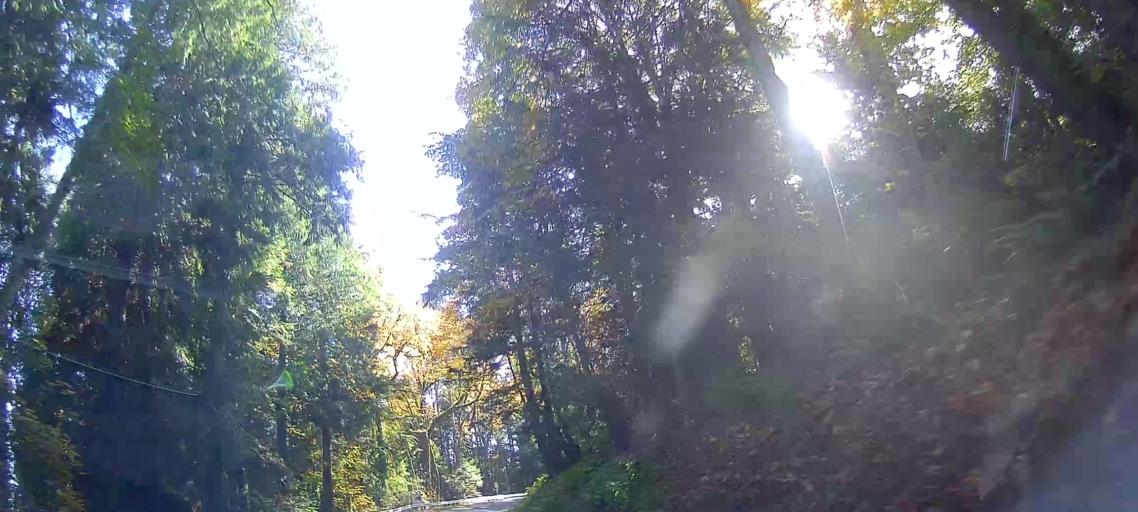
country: US
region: Washington
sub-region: Snohomish County
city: Stanwood
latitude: 48.2320
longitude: -122.4563
